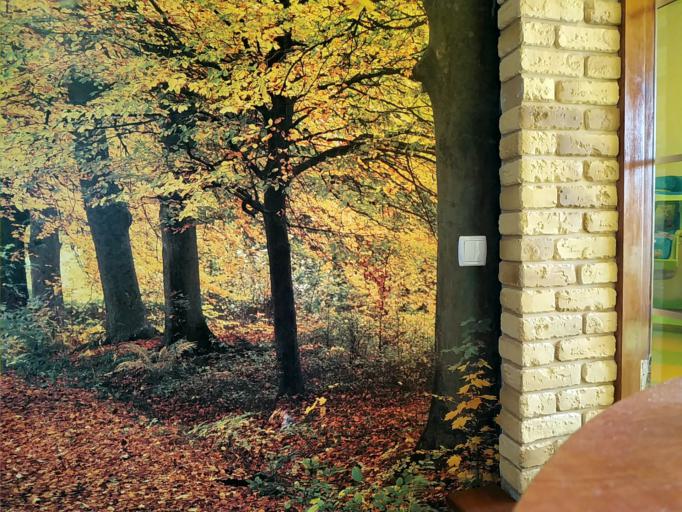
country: RU
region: Novgorod
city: Staraya Russa
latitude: 57.8373
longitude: 31.4658
